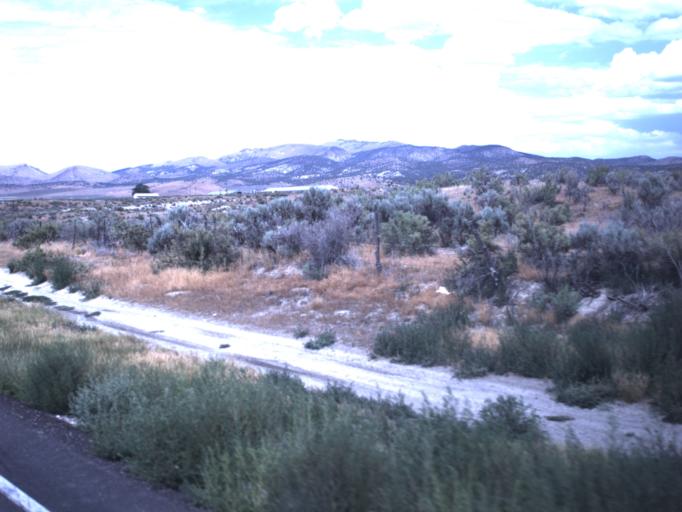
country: US
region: Utah
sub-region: Sanpete County
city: Moroni
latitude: 39.5515
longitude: -111.5998
